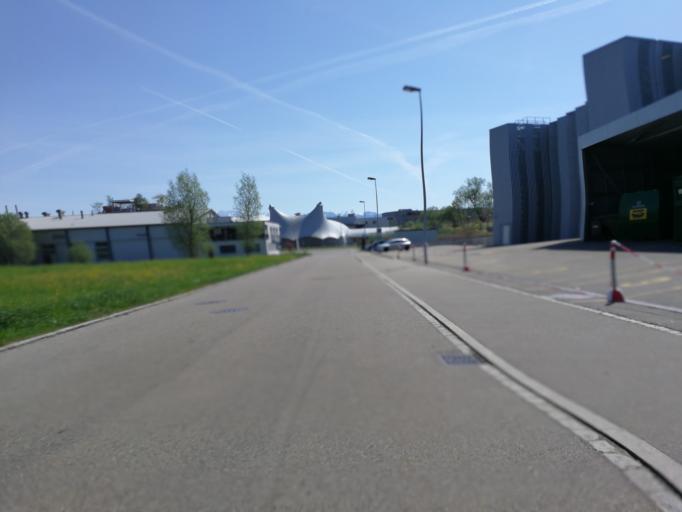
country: CH
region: Zurich
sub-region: Bezirk Hinwil
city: Bubikon
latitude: 47.2787
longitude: 8.8184
